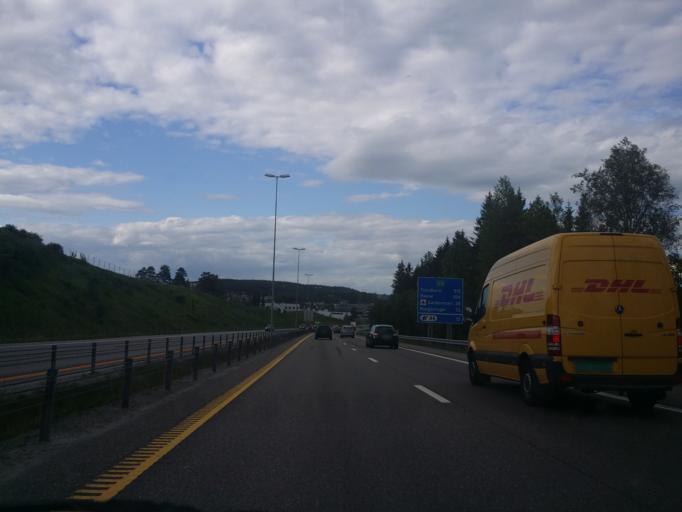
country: NO
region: Akershus
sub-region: Skedsmo
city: Leirsund
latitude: 60.0026
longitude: 11.0459
